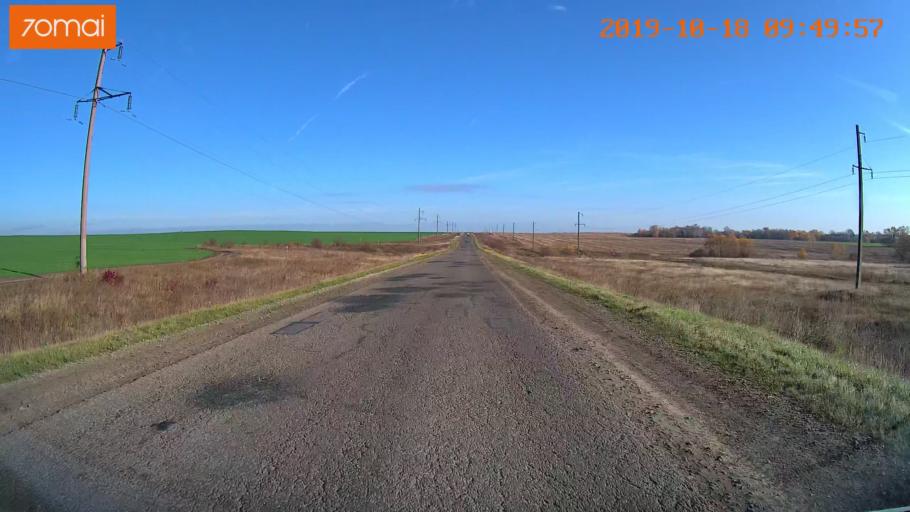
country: RU
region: Tula
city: Kazachka
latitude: 53.3235
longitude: 38.2707
